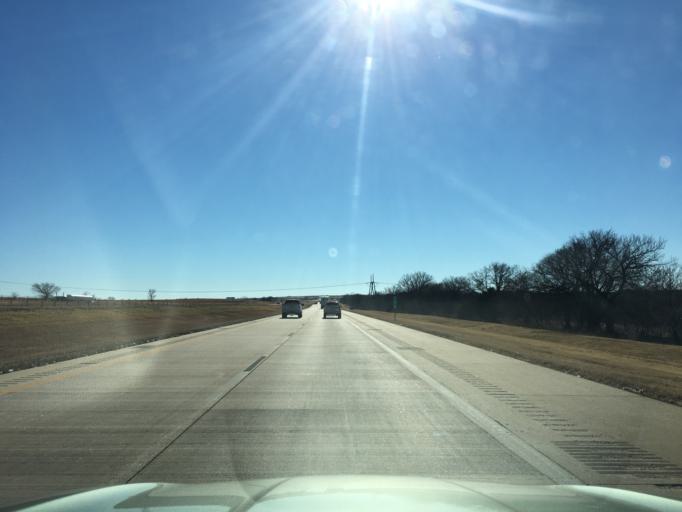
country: US
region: Oklahoma
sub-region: Noble County
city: Perry
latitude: 36.4276
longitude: -97.3272
